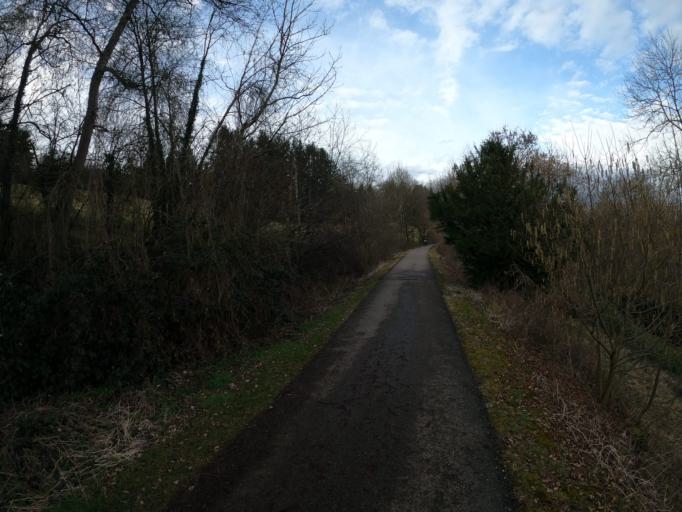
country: DE
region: Baden-Wuerttemberg
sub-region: Regierungsbezirk Stuttgart
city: Rechberghausen
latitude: 48.7181
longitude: 9.6304
